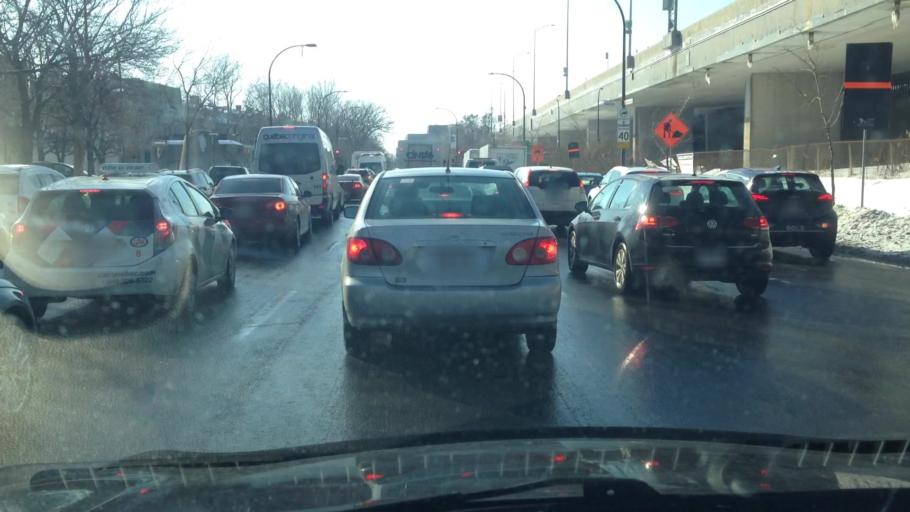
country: CA
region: Quebec
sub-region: Montreal
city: Montreal
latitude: 45.4896
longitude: -73.5759
